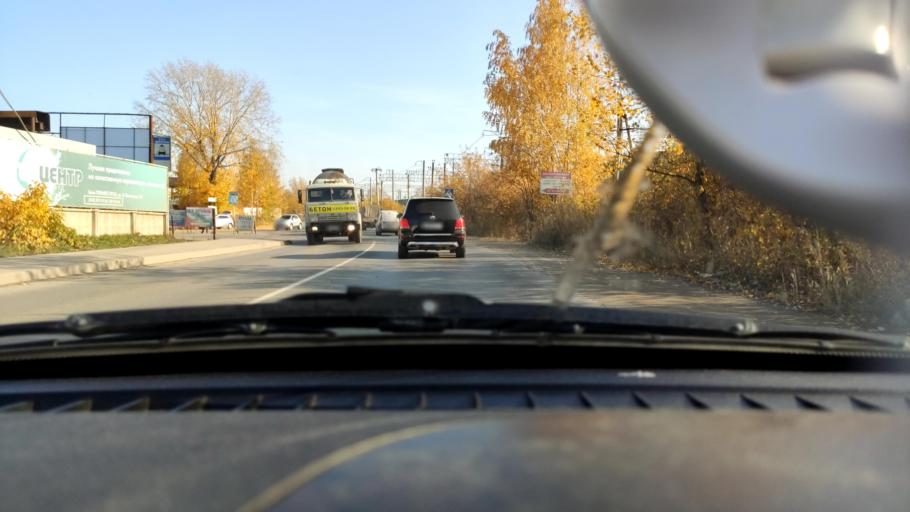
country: RU
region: Perm
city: Froly
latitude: 57.9545
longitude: 56.2221
